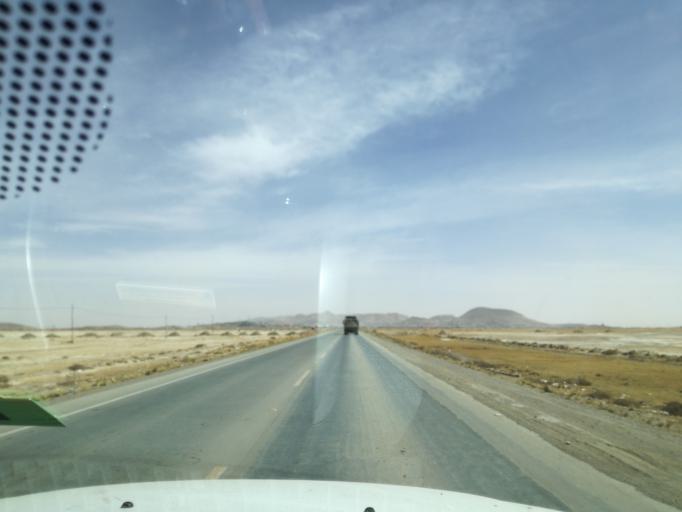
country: BO
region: Oruro
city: Oruro
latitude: -17.9018
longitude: -67.0532
